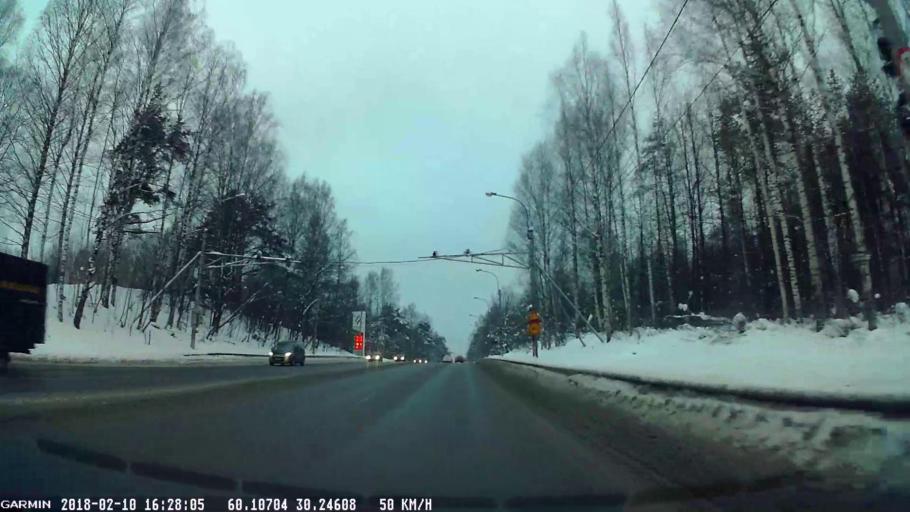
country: RU
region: St.-Petersburg
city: Levashovo
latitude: 60.1074
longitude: 30.2457
